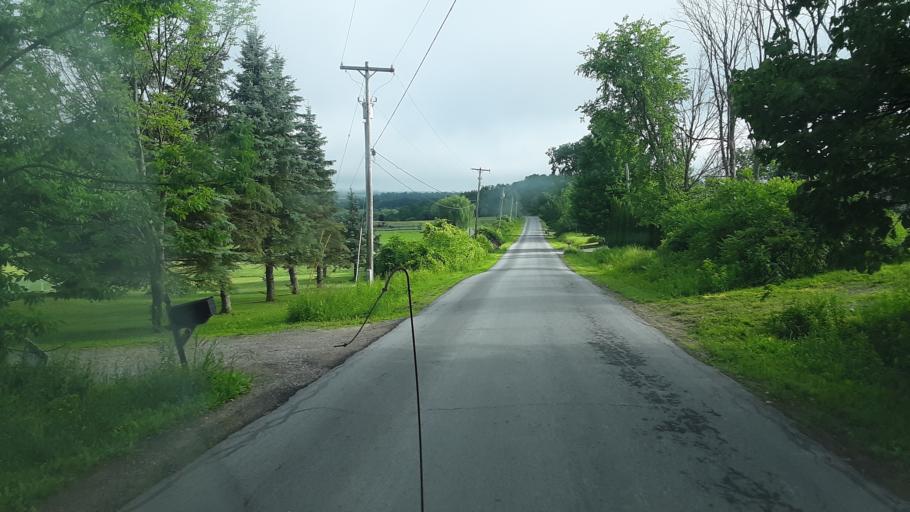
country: US
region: New York
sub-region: Montgomery County
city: Fonda
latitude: 42.8720
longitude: -74.3772
